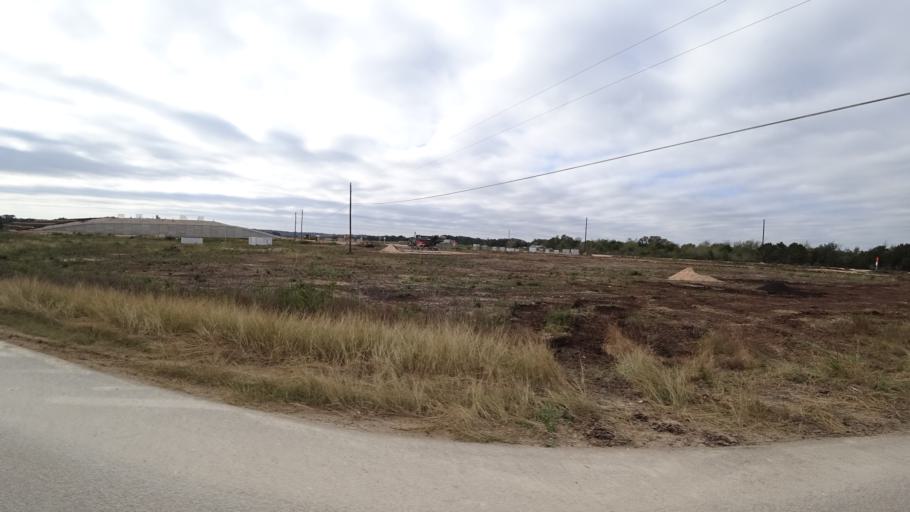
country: US
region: Texas
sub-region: Travis County
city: Shady Hollow
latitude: 30.1381
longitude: -97.8648
